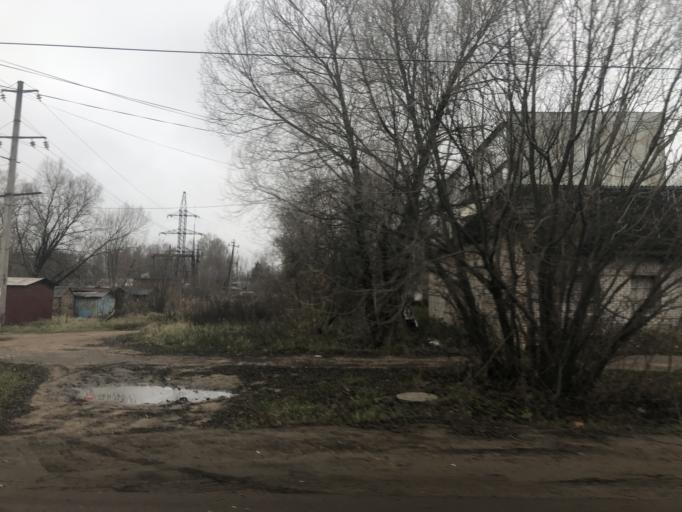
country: RU
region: Tverskaya
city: Rzhev
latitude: 56.2770
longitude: 34.2962
